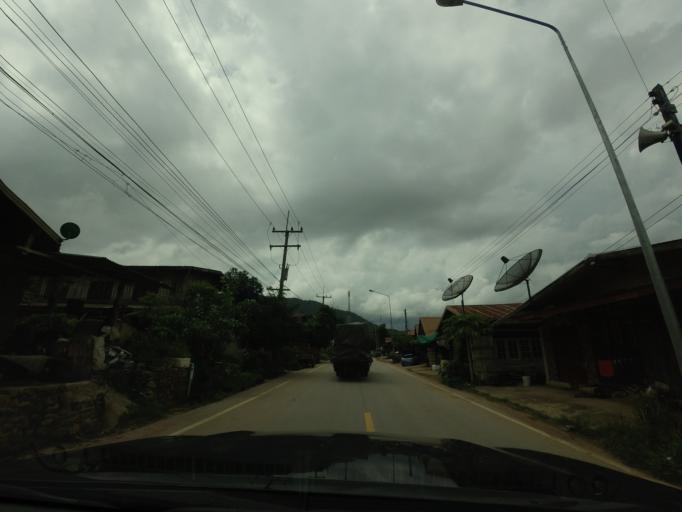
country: TH
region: Loei
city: Pak Chom
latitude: 18.0567
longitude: 101.8043
